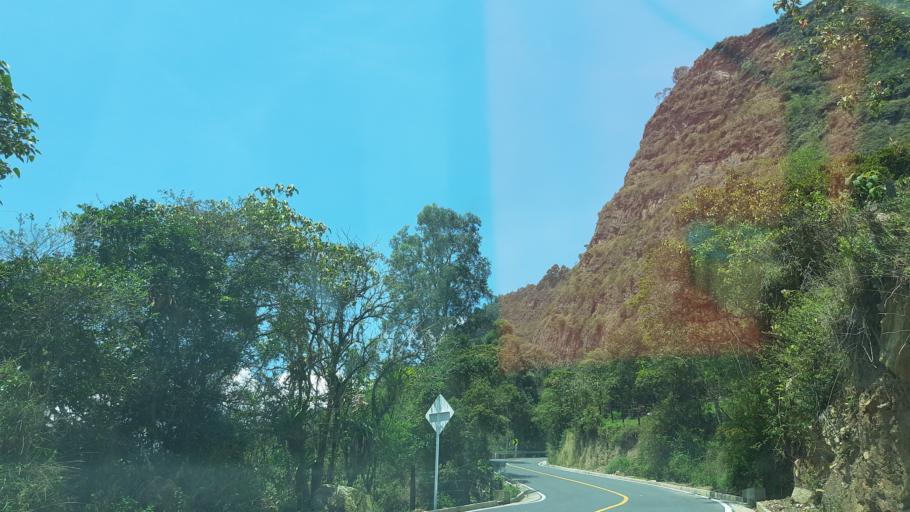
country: CO
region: Boyaca
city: Chinavita
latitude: 5.1306
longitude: -73.3872
